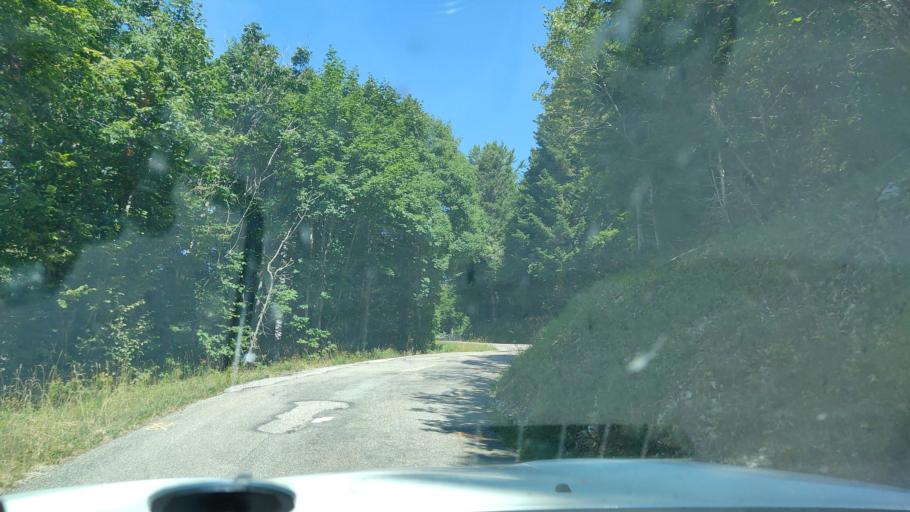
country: FR
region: Rhone-Alpes
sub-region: Departement de la Savoie
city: Le Bourget-du-Lac
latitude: 45.6527
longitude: 5.8101
